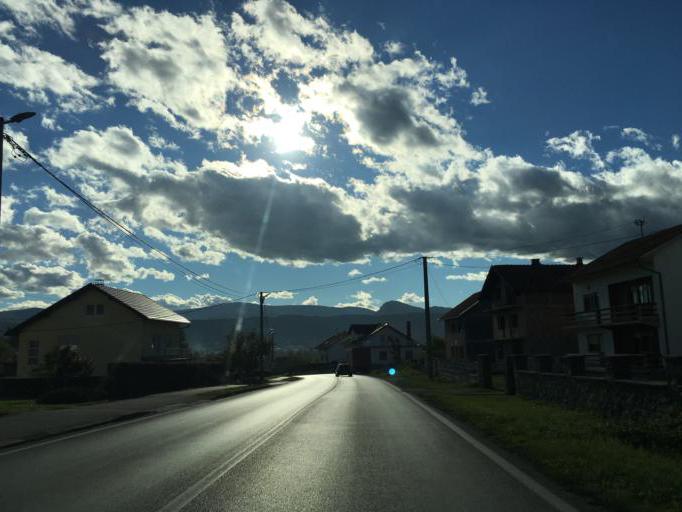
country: BA
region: Federation of Bosnia and Herzegovina
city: Bugojno
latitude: 44.0623
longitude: 17.4682
